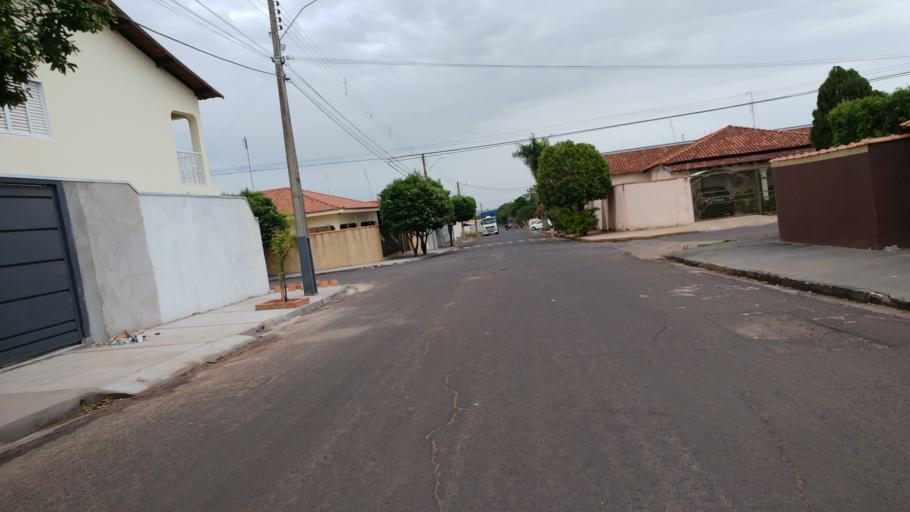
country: BR
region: Sao Paulo
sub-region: Paraguacu Paulista
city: Paraguacu Paulista
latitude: -22.4146
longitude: -50.5875
